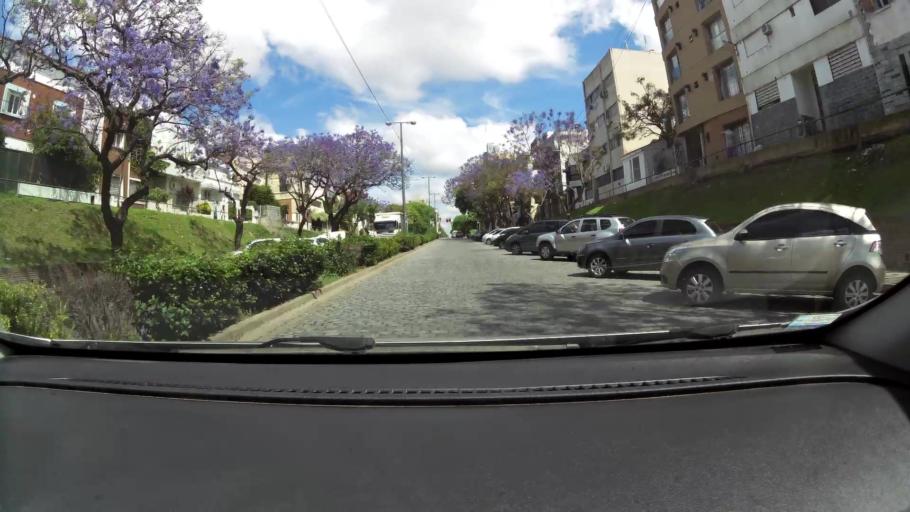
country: AR
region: Santa Fe
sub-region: Departamento de Rosario
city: Rosario
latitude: -32.9600
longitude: -60.6257
